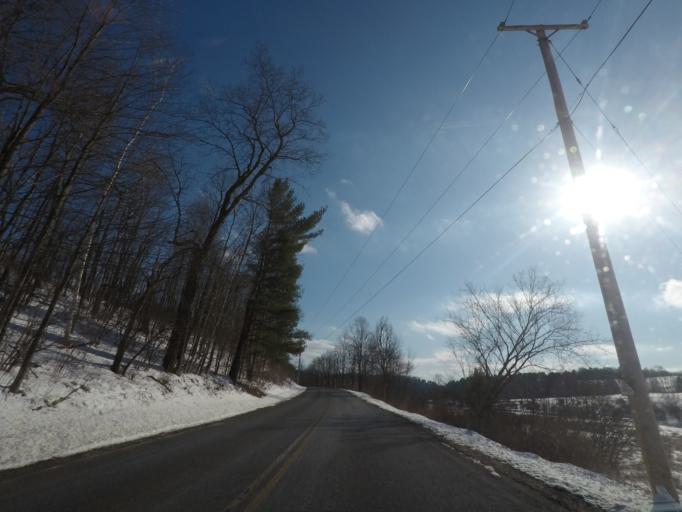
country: US
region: New York
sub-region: Rensselaer County
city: Hoosick Falls
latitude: 42.8815
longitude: -73.4986
